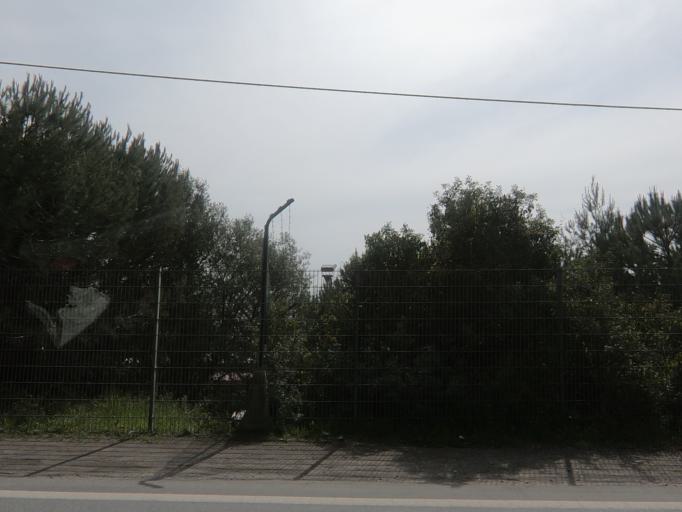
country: PT
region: Setubal
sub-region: Setubal
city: Setubal
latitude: 38.4976
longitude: -8.9306
